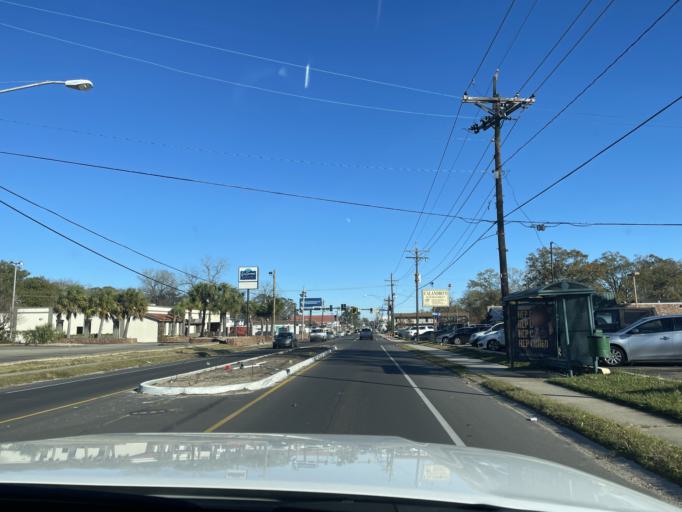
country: US
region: Louisiana
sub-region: East Baton Rouge Parish
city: Baton Rouge
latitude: 30.4443
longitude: -91.1485
